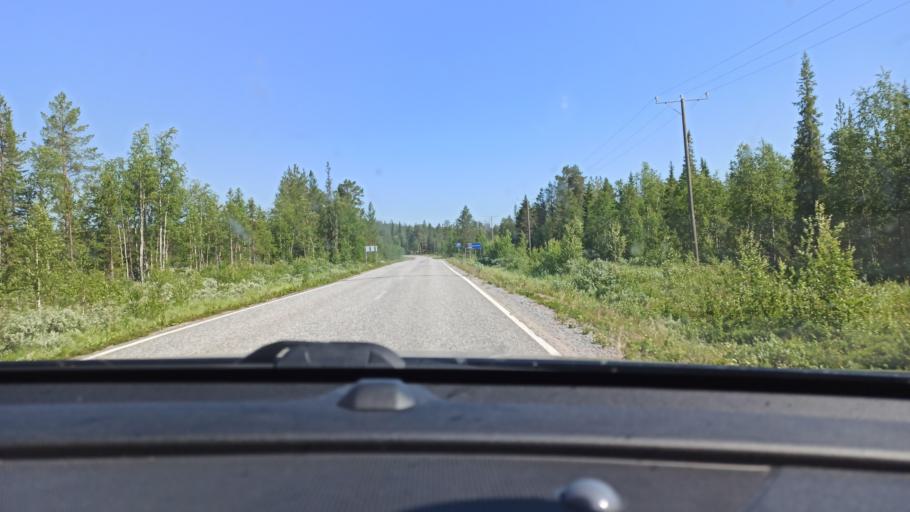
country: FI
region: Lapland
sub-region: Tunturi-Lappi
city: Kolari
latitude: 67.6309
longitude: 24.1573
